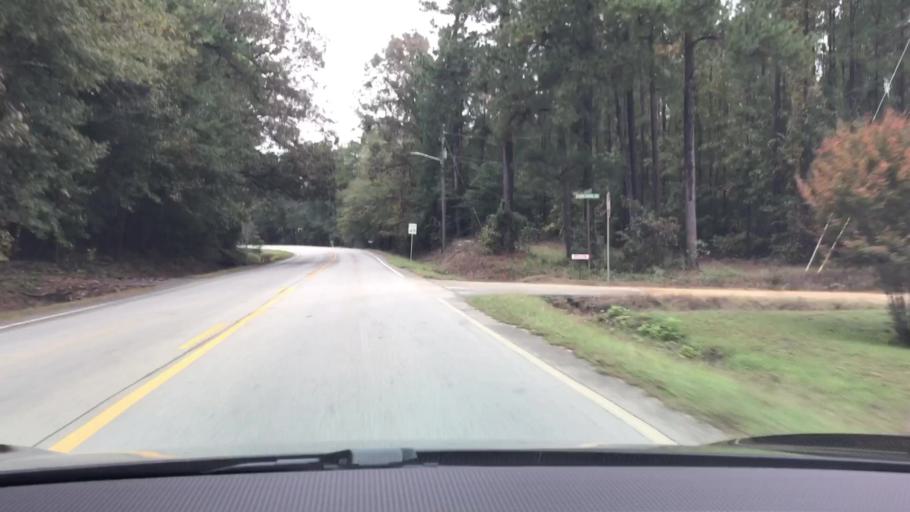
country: US
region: Georgia
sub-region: Jefferson County
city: Wrens
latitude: 33.2064
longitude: -82.4688
